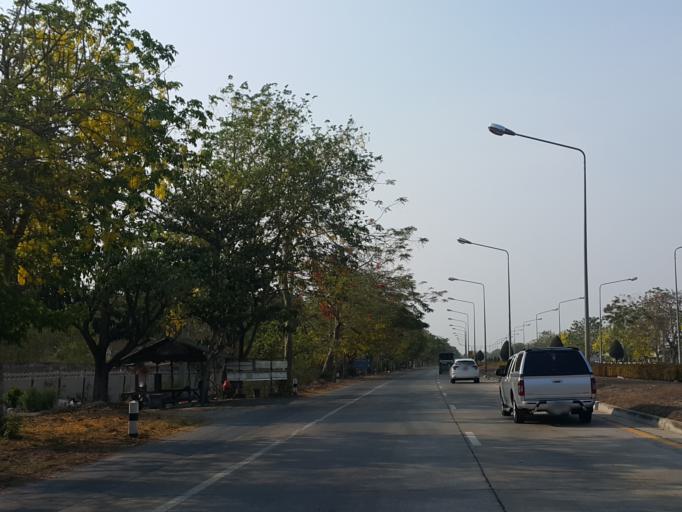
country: TH
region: Suphan Buri
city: Sam Chuk
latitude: 14.7655
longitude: 100.0932
